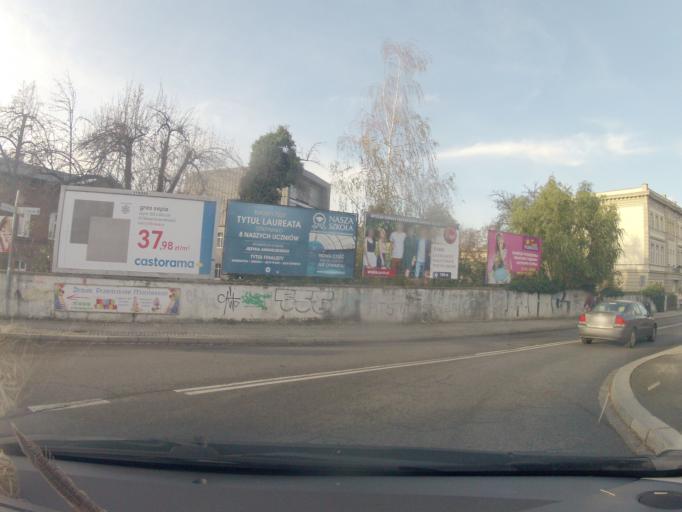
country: PL
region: Opole Voivodeship
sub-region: Powiat opolski
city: Opole
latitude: 50.6629
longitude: 17.9219
